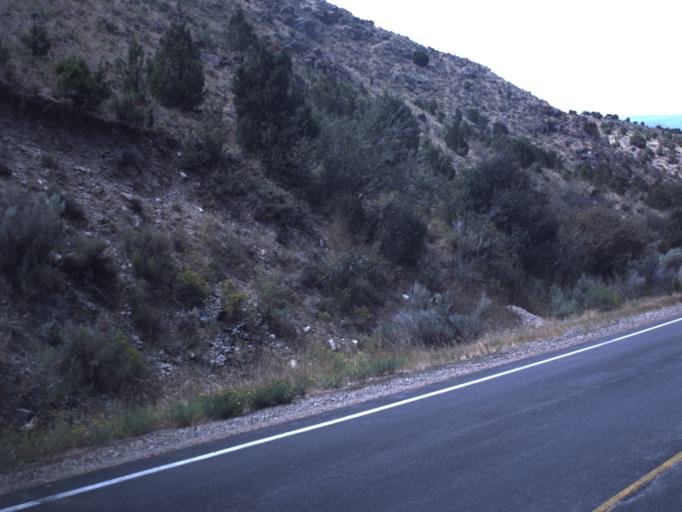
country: US
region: Utah
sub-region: Rich County
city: Randolph
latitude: 41.8239
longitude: -111.3051
